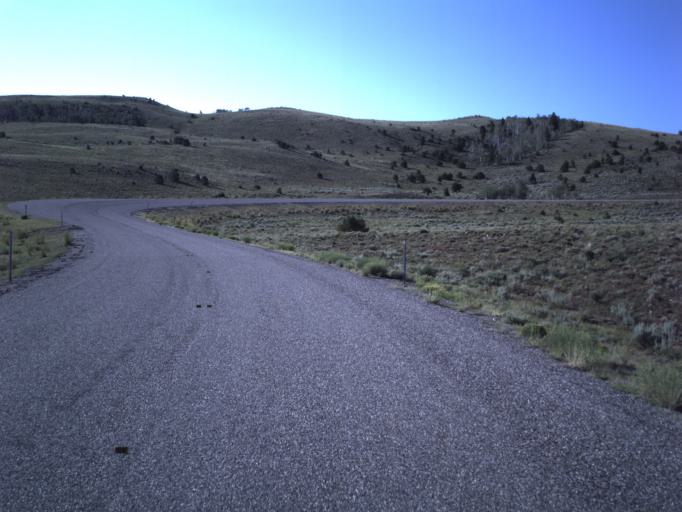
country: US
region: Utah
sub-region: Wayne County
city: Loa
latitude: 38.6029
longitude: -111.4618
